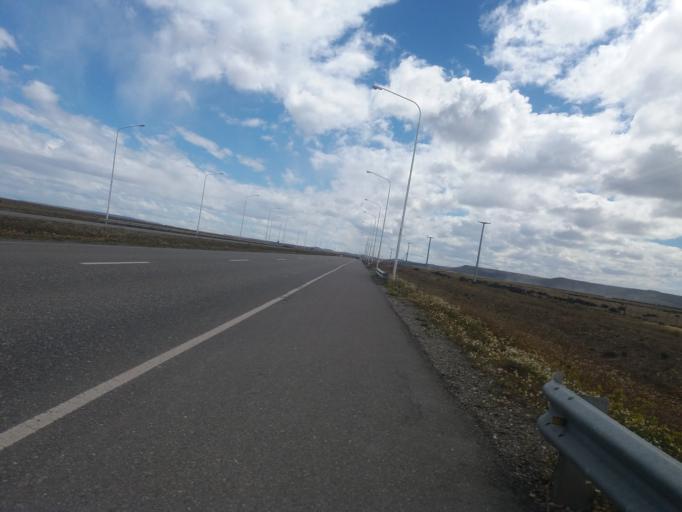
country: AR
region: Santa Cruz
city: Rio Gallegos
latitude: -51.6217
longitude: -69.4761
